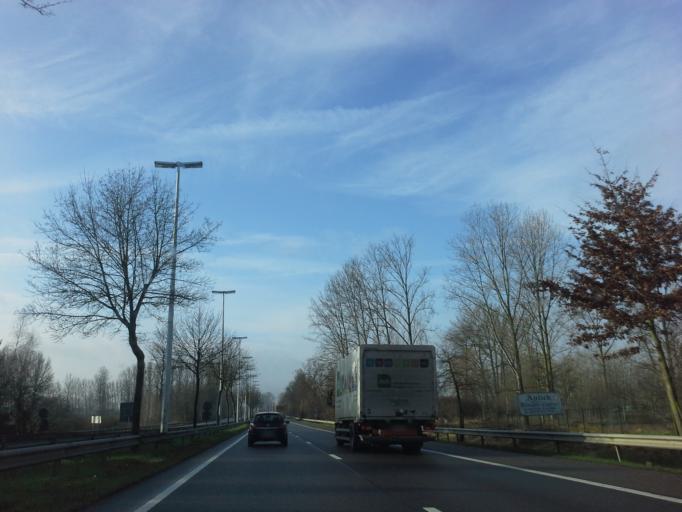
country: BE
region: Flanders
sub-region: Provincie Limburg
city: Alken
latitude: 50.8935
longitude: 5.3142
